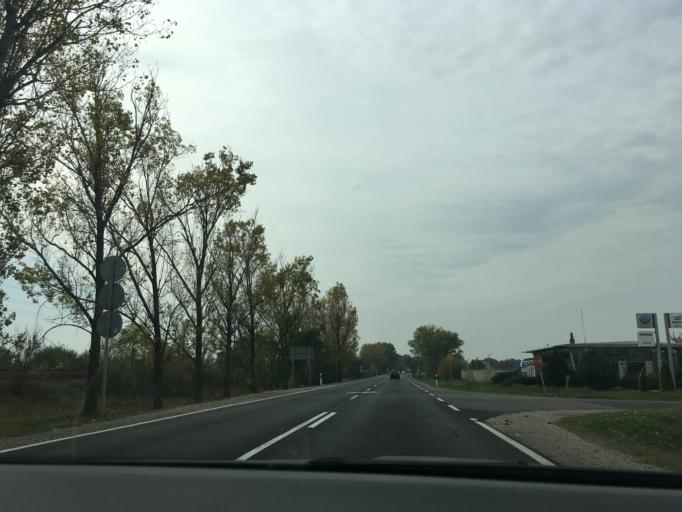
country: HU
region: Hajdu-Bihar
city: Debrecen
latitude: 47.5034
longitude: 21.5879
